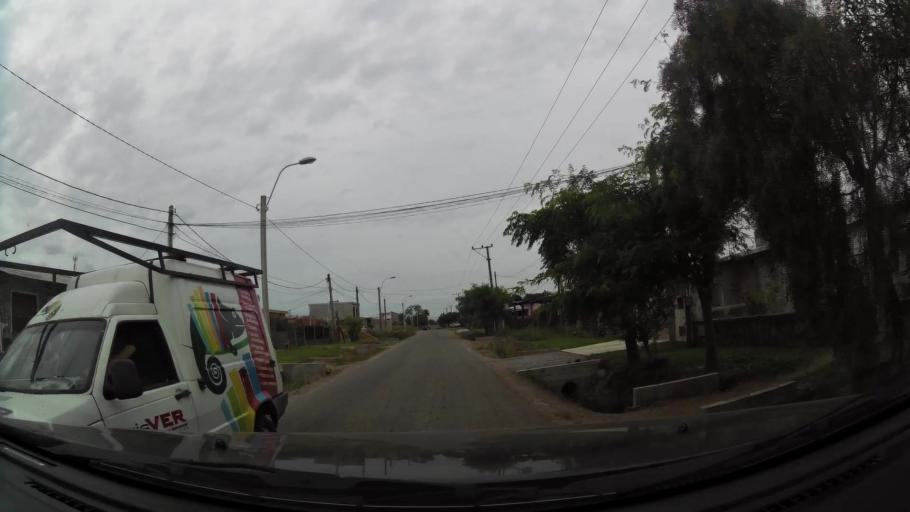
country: UY
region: Canelones
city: Las Piedras
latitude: -34.7208
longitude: -56.2035
